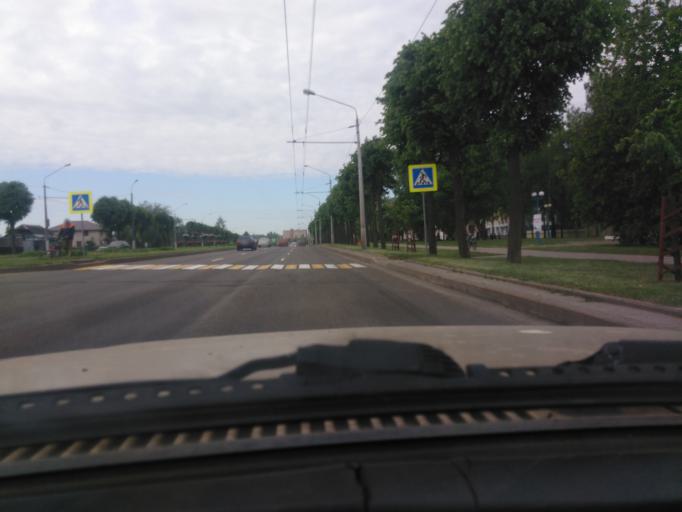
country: BY
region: Mogilev
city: Mahilyow
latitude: 53.9043
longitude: 30.3037
